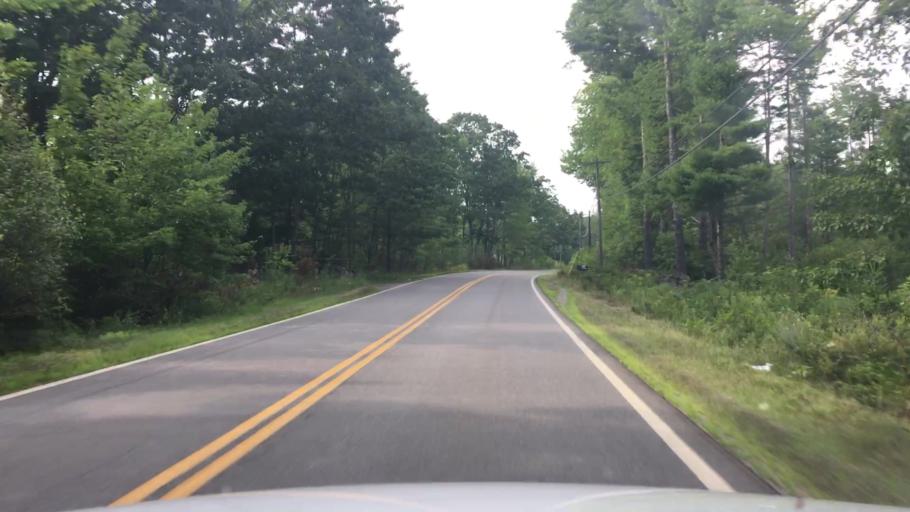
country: US
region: Maine
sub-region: Lincoln County
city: Waldoboro
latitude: 44.1449
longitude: -69.3737
